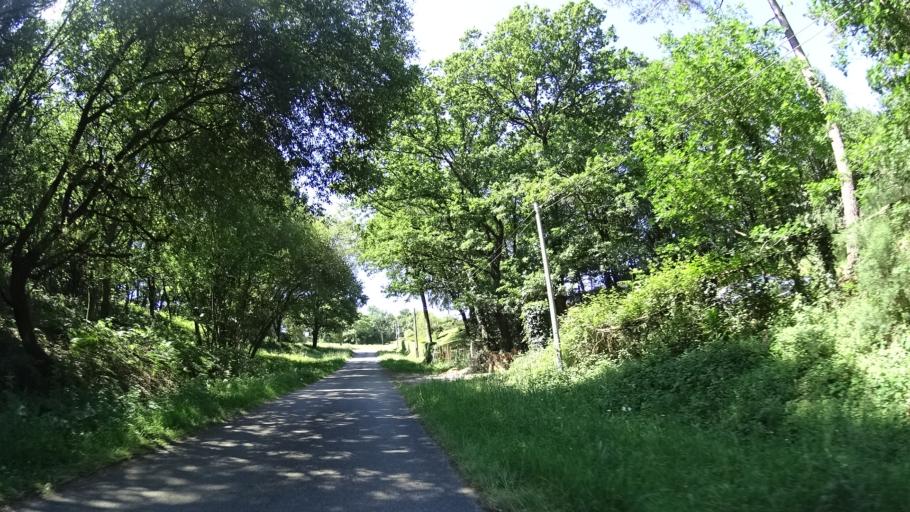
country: FR
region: Brittany
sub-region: Departement d'Ille-et-Vilaine
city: Langon
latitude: 47.7623
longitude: -1.8350
